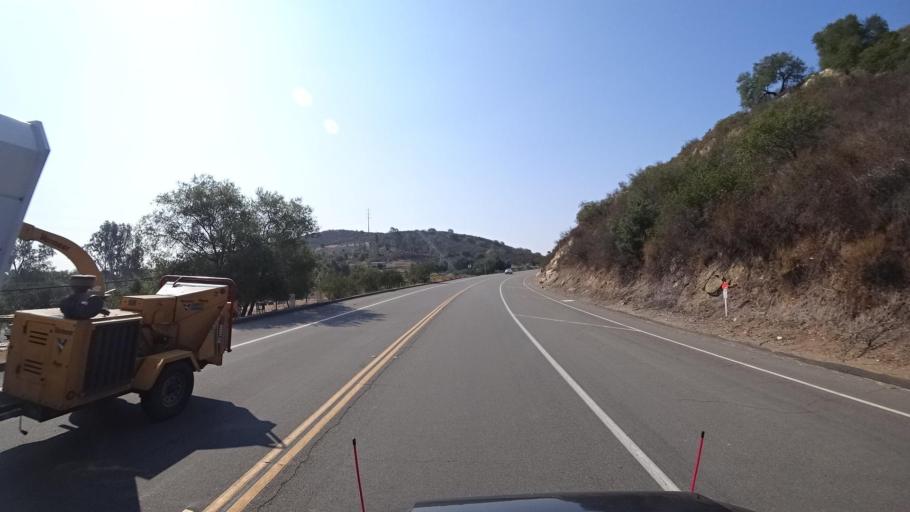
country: US
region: California
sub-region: San Diego County
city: Escondido
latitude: 33.1690
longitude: -117.1054
